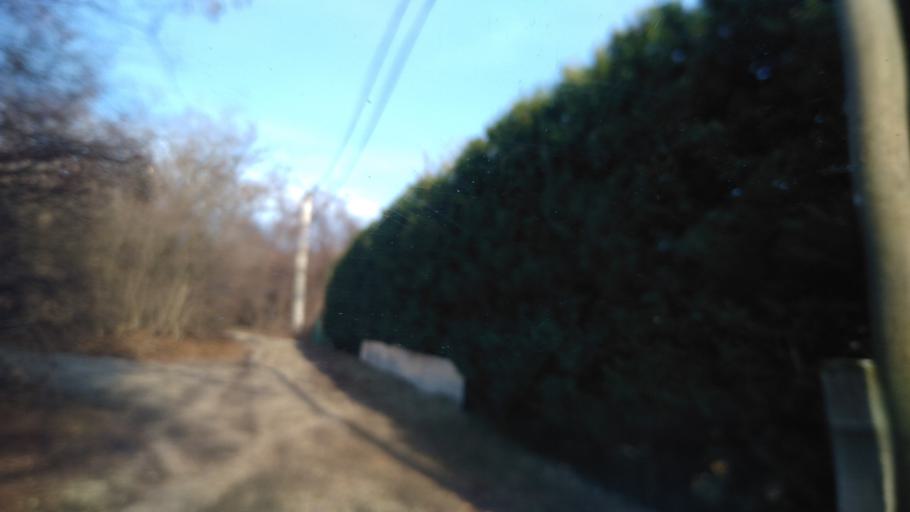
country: HU
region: Pest
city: Szentendre
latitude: 47.6932
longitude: 19.0586
